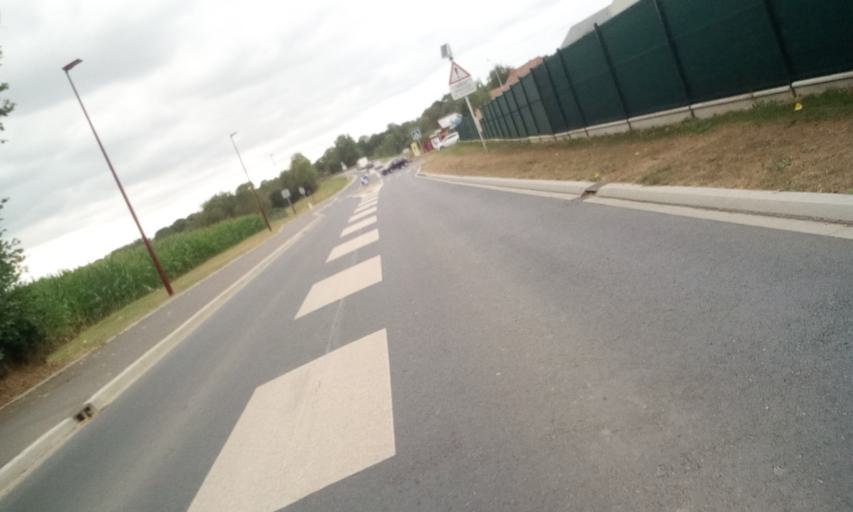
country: FR
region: Lower Normandy
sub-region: Departement du Calvados
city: Troarn
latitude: 49.1863
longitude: -0.1891
